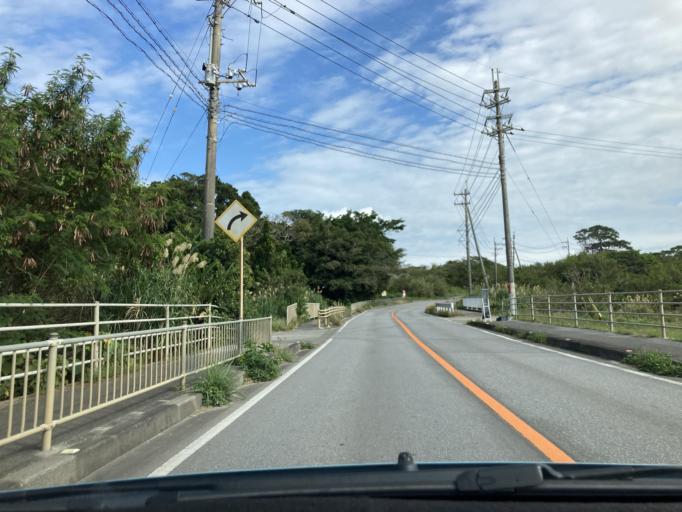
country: JP
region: Okinawa
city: Nago
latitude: 26.6992
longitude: 127.9320
